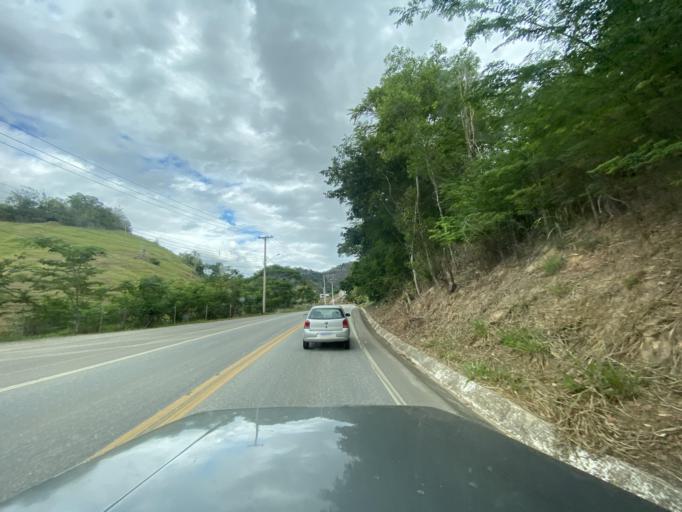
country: BR
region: Espirito Santo
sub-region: Jeronimo Monteiro
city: Jeronimo Monteiro
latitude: -20.7642
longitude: -41.4474
